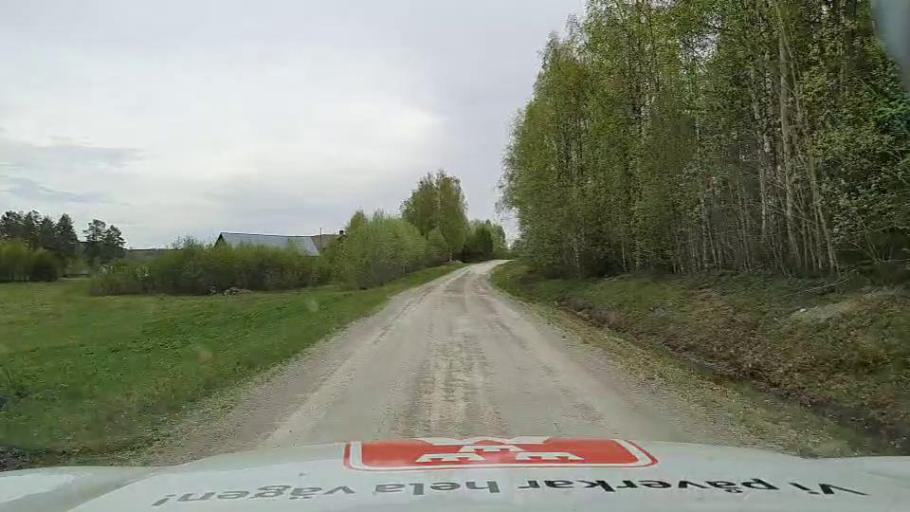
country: SE
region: Jaemtland
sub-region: Bergs Kommun
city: Hoverberg
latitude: 62.6832
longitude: 14.7743
